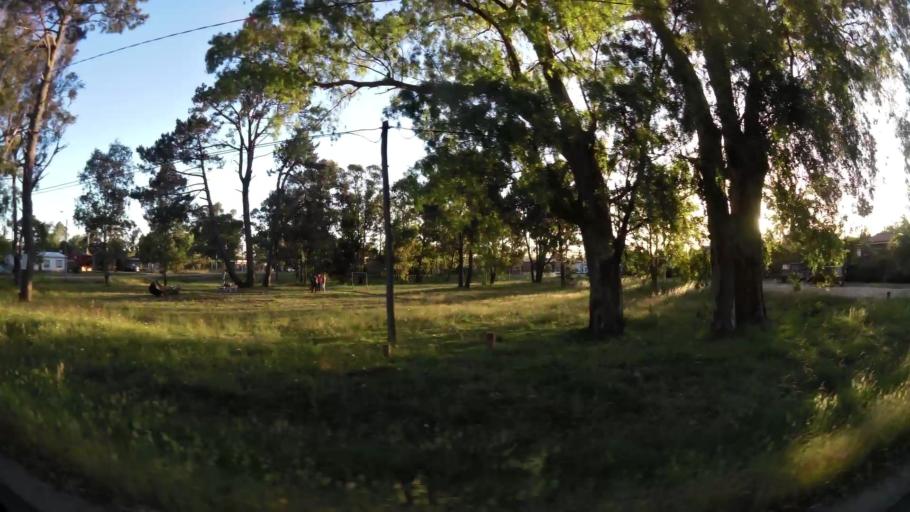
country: UY
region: Canelones
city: Barra de Carrasco
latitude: -34.8457
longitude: -56.0078
